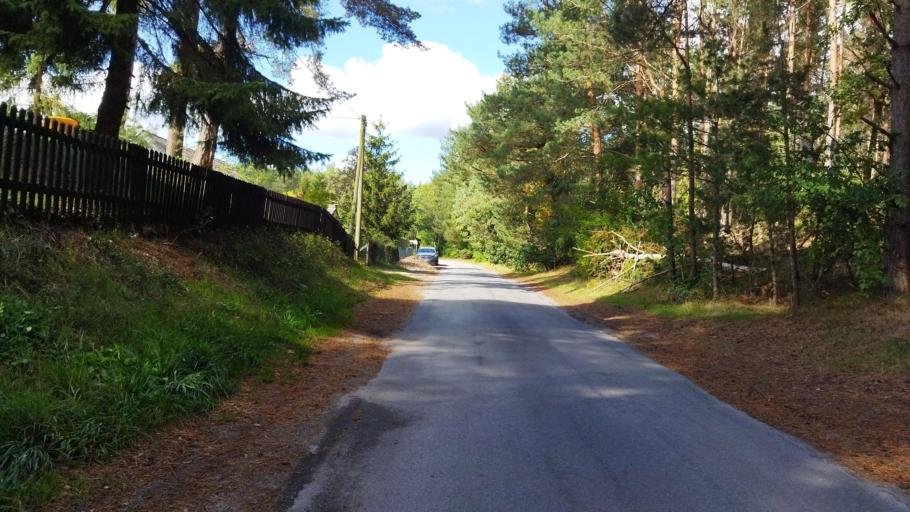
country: DE
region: Lower Saxony
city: Emsburen
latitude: 52.4280
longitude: 7.3417
